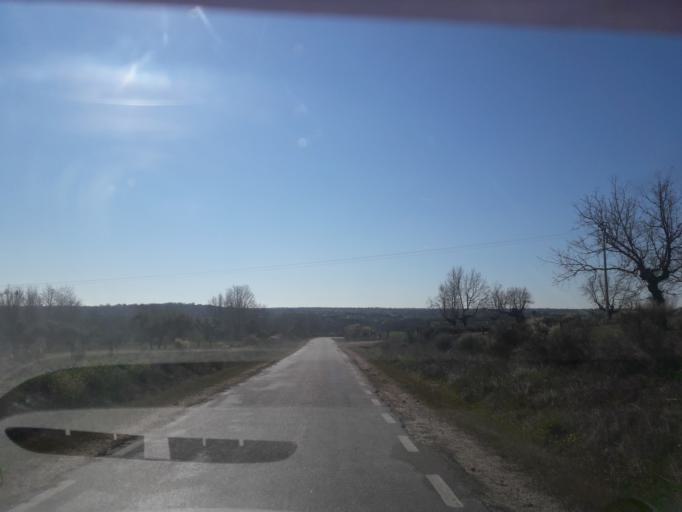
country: ES
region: Castille and Leon
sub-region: Provincia de Salamanca
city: Valsalabroso
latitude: 41.1646
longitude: -6.4990
